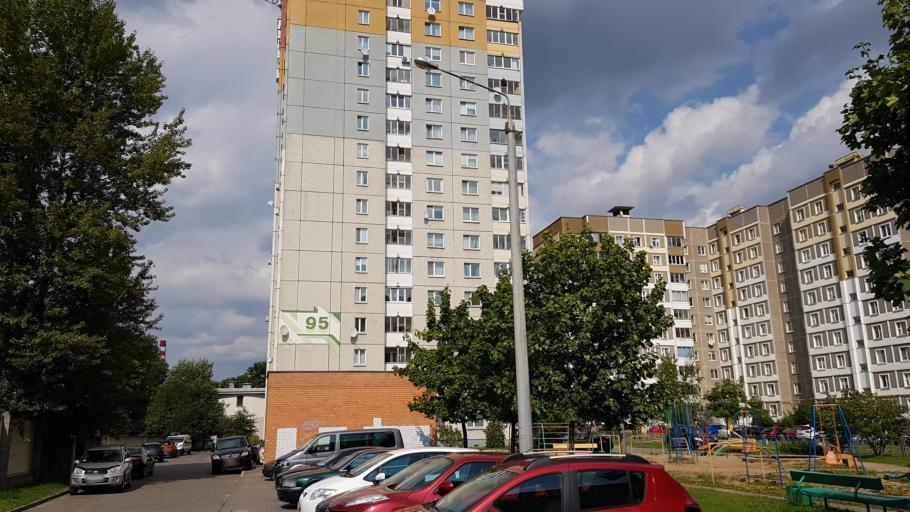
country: BY
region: Minsk
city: Minsk
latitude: 53.9206
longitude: 27.5610
